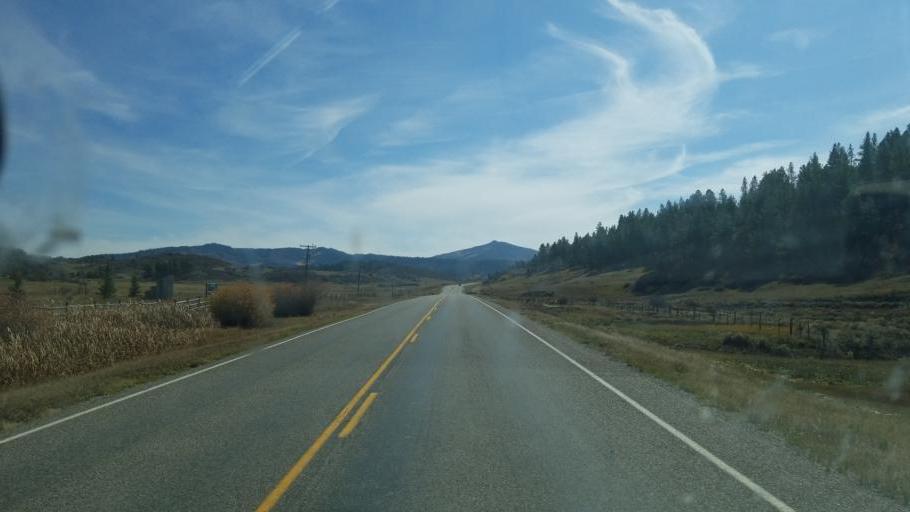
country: US
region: New Mexico
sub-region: Rio Arriba County
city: Dulce
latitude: 37.0183
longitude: -106.8122
